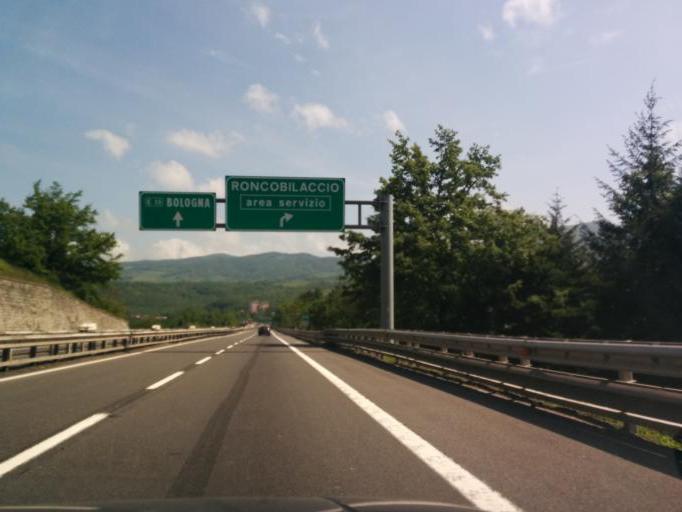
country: IT
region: Emilia-Romagna
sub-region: Provincia di Bologna
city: Castiglione dei Pepoli
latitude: 44.1075
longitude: 11.2255
